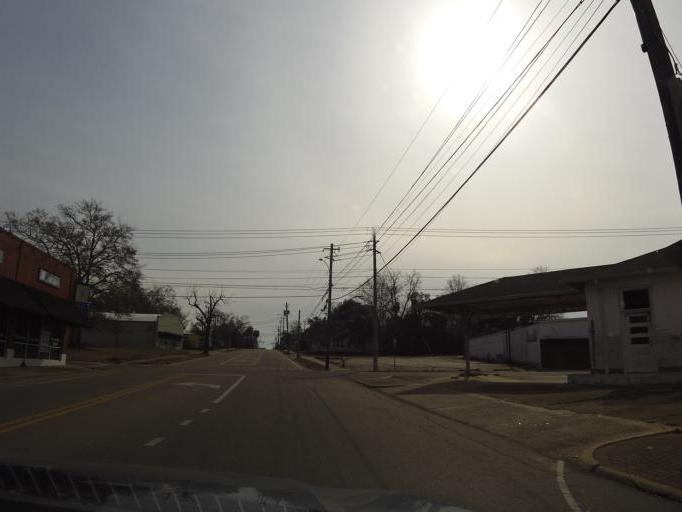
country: US
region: Alabama
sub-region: Houston County
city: Dothan
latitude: 31.2222
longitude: -85.3906
